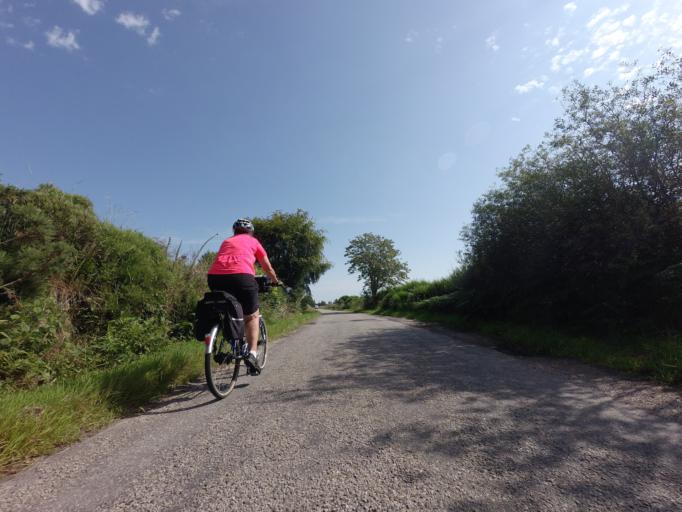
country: GB
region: Scotland
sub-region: Highland
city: Invergordon
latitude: 57.7229
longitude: -4.2019
